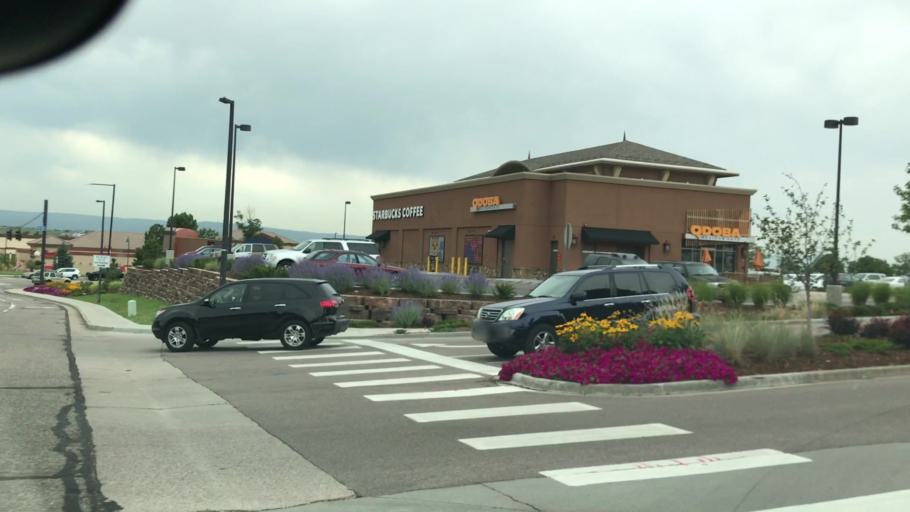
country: US
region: Colorado
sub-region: Douglas County
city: Castle Rock
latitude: 39.4130
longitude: -104.8728
